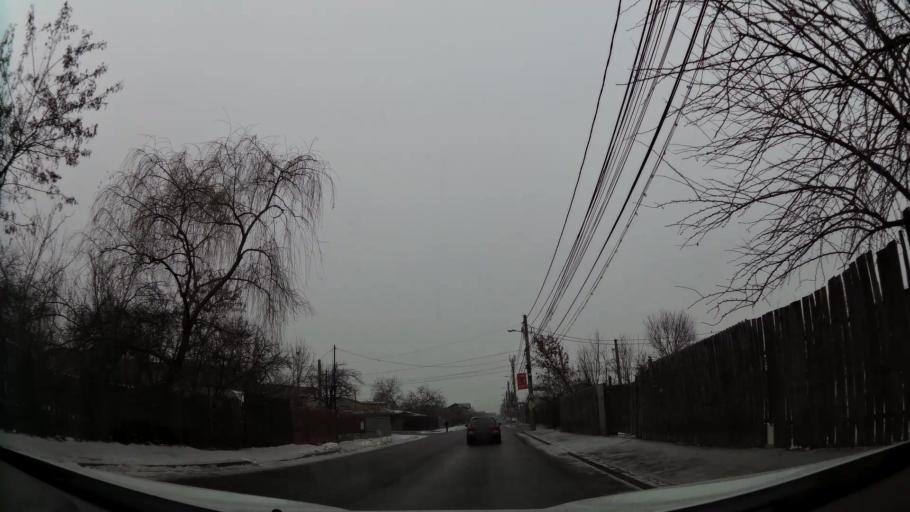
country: RO
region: Prahova
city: Ploiesti
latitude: 44.9531
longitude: 26.0438
